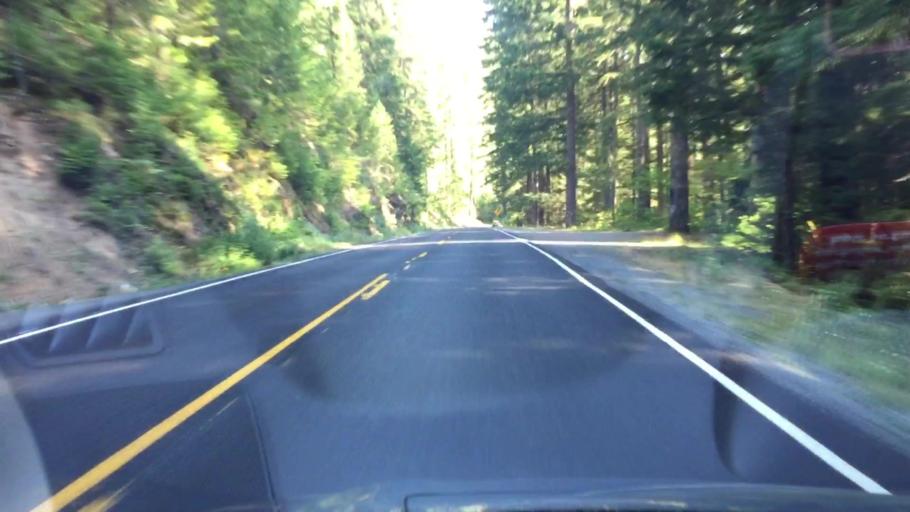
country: US
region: Washington
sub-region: Pierce County
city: Buckley
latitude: 46.7136
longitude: -121.5759
